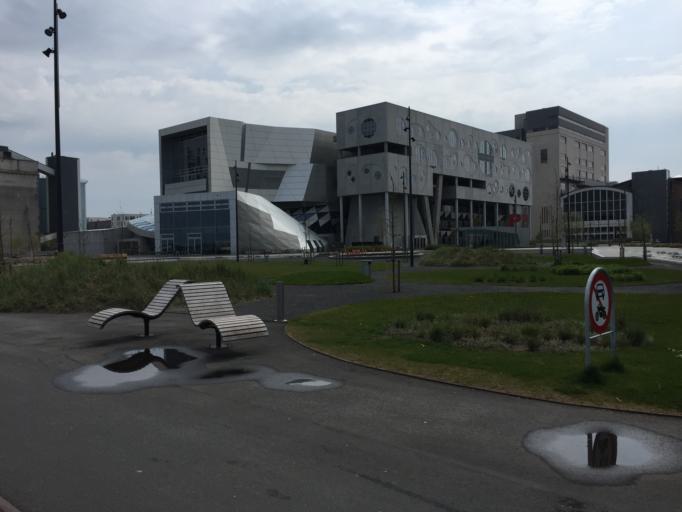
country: DK
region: North Denmark
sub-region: Alborg Kommune
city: Aalborg
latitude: 57.0486
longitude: 9.9318
